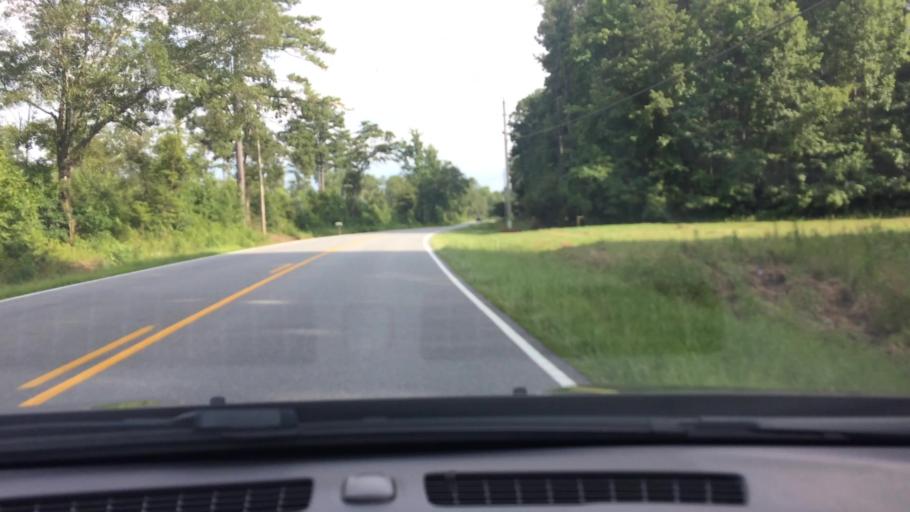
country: US
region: North Carolina
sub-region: Pitt County
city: Winterville
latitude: 35.5131
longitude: -77.3821
